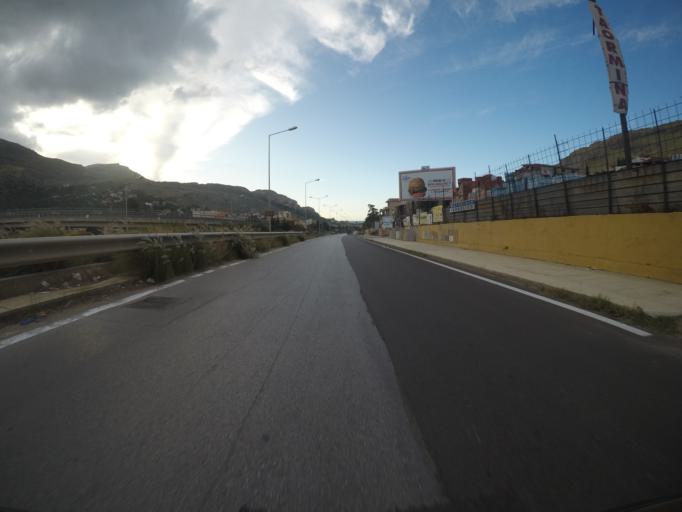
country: IT
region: Sicily
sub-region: Palermo
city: Isola delle Femmine
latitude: 38.1929
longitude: 13.2873
